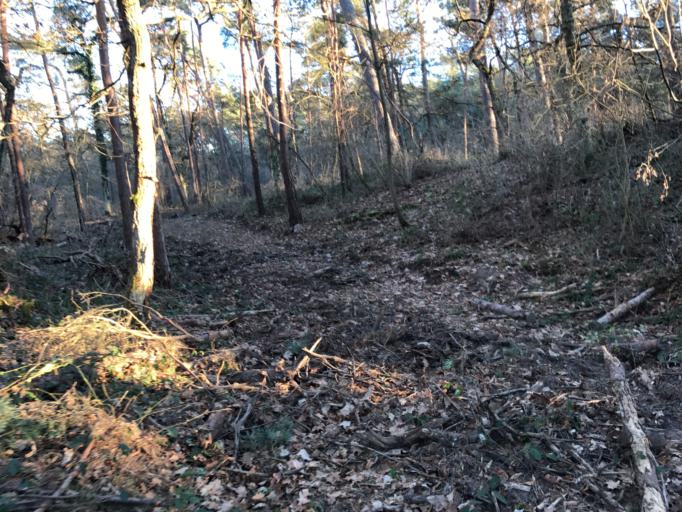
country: DE
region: Rheinland-Pfalz
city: Budenheim
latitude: 50.0107
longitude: 8.1573
